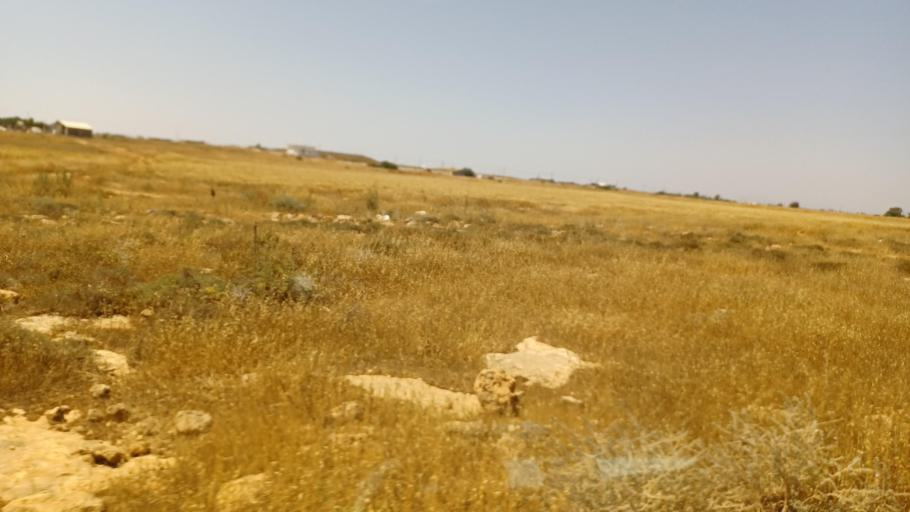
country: CY
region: Ammochostos
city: Liopetri
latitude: 35.0307
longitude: 33.8882
